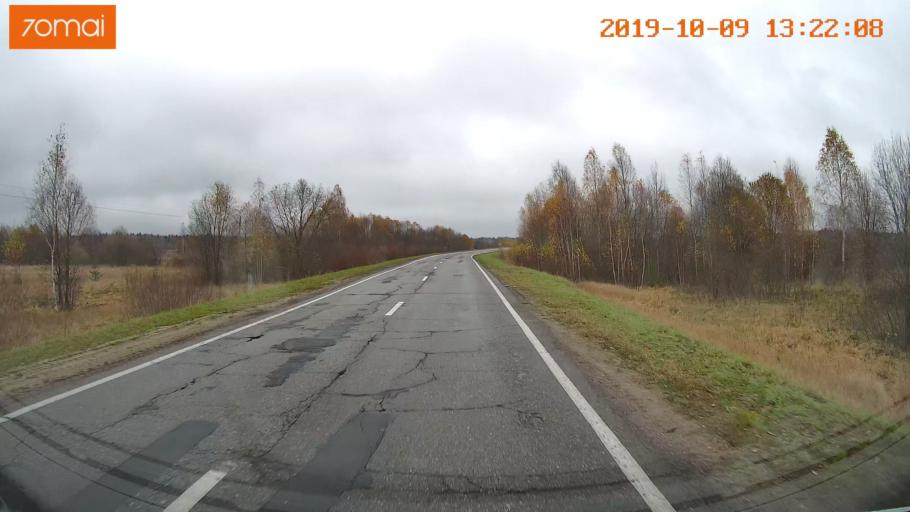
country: RU
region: Jaroslavl
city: Lyubim
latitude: 58.3408
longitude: 40.8585
